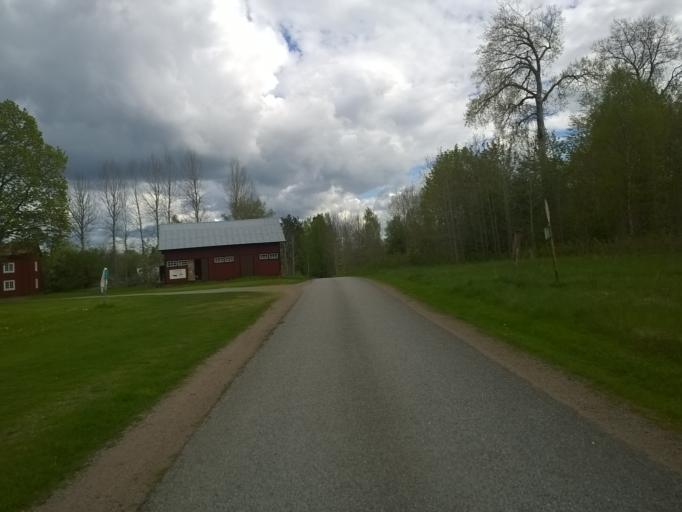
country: SE
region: Joenkoeping
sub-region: Eksjo Kommun
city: Eksjoe
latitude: 57.6442
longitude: 14.9821
